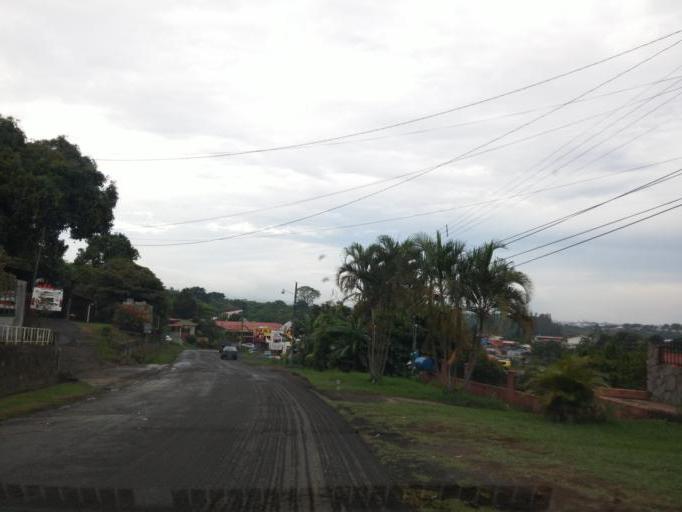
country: CR
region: Alajuela
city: San Juan
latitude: 10.0821
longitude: -84.3392
